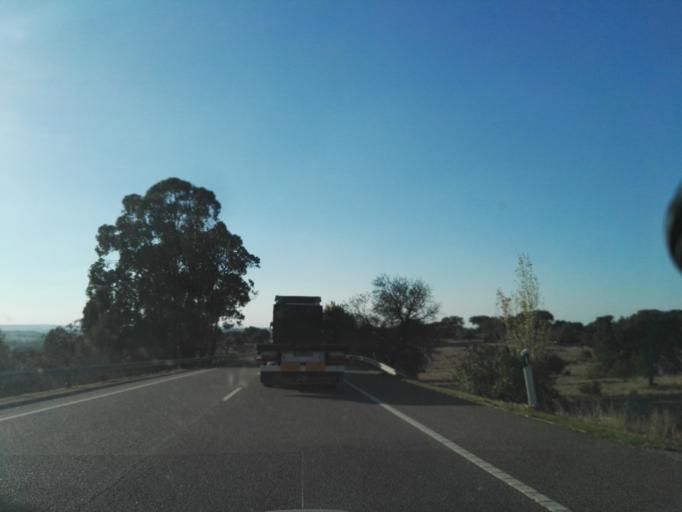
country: PT
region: Portalegre
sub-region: Elvas
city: Elvas
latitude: 38.8606
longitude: -7.2943
